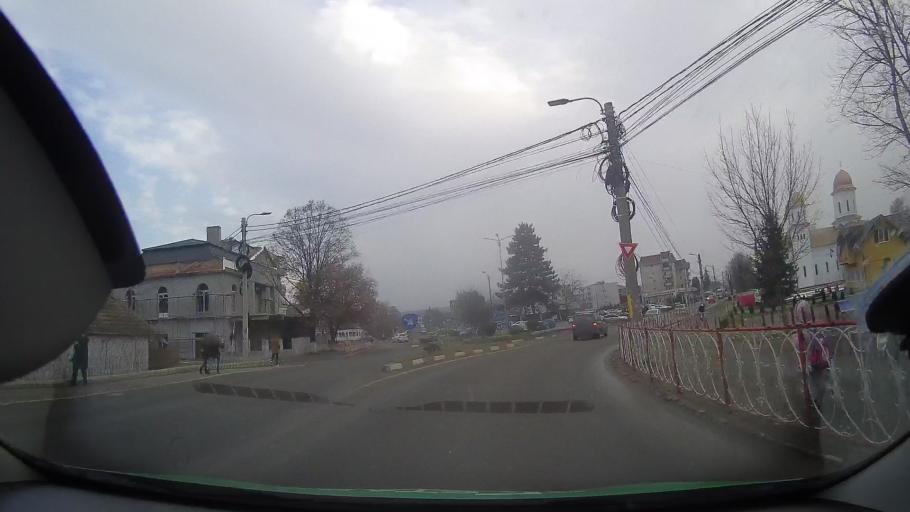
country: RO
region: Mures
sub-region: Municipiul Tarnaveni
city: Tarnaveni
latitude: 46.3319
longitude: 24.2948
